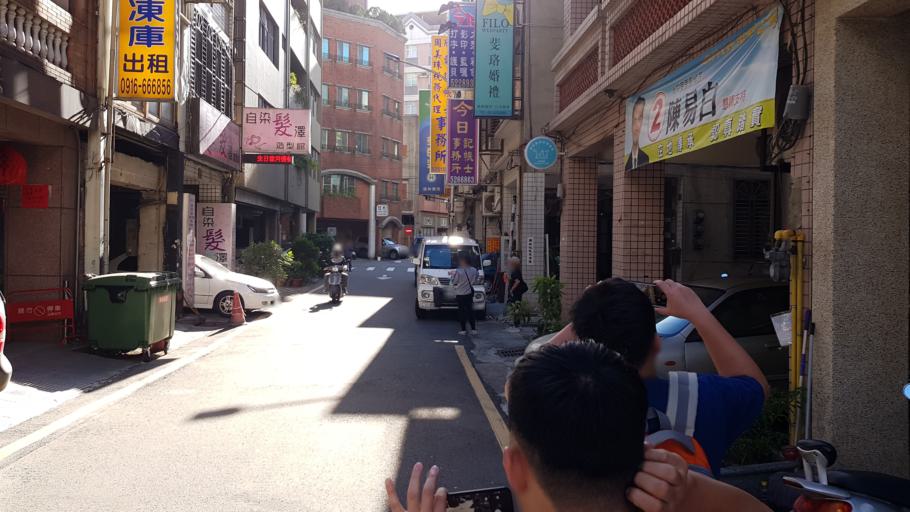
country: TW
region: Taiwan
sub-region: Hsinchu
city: Hsinchu
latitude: 24.8074
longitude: 120.9672
